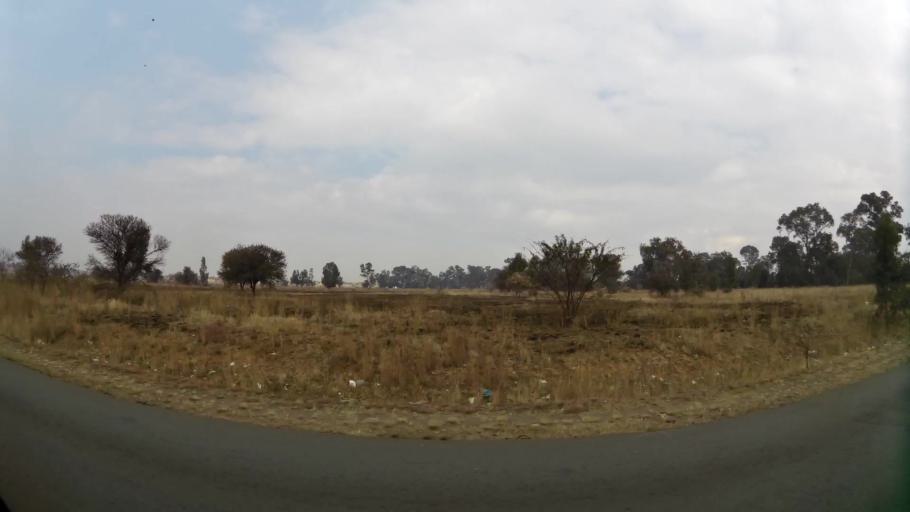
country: ZA
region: Gauteng
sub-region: Sedibeng District Municipality
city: Vanderbijlpark
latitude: -26.6744
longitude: 27.8405
